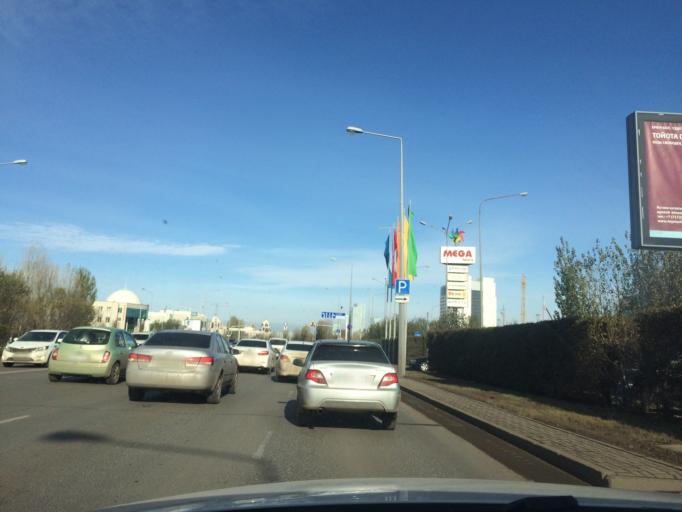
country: KZ
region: Astana Qalasy
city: Astana
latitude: 51.1446
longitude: 71.4116
